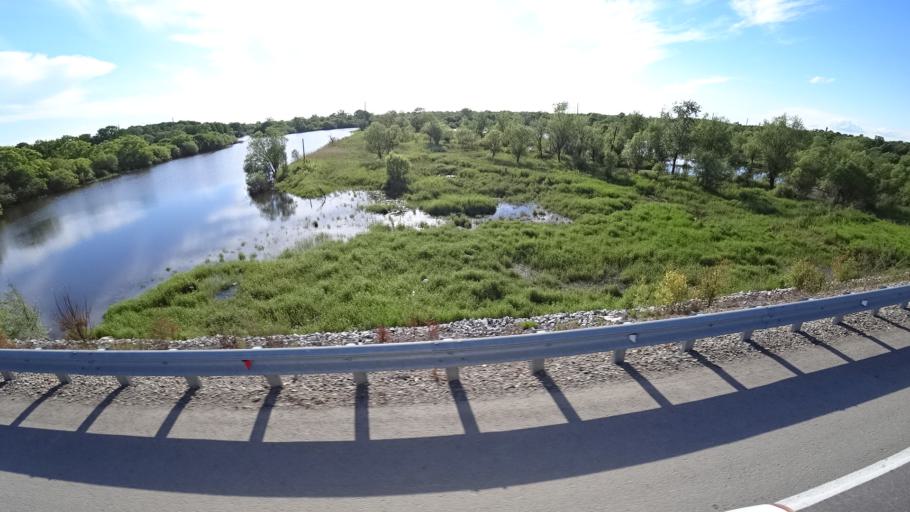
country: RU
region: Khabarovsk Krai
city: Khor
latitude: 47.8603
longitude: 134.9628
